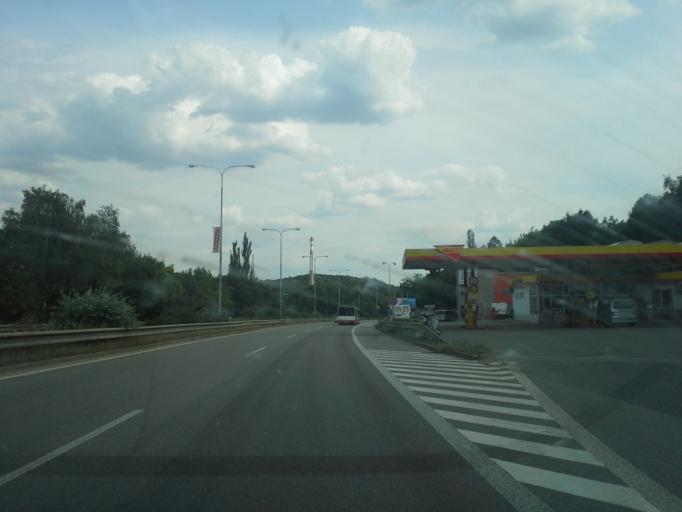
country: CZ
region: South Moravian
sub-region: Mesto Brno
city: Mokra Hora
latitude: 49.2550
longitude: 16.5857
